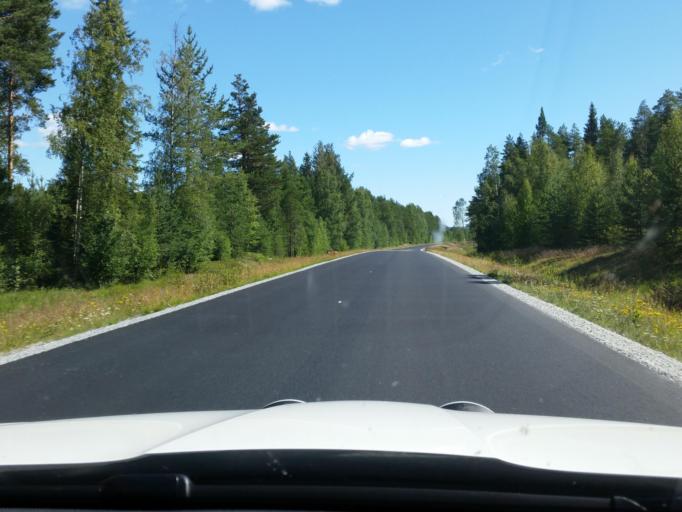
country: SE
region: Norrbotten
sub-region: Pitea Kommun
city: Roknas
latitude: 65.3398
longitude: 21.1579
